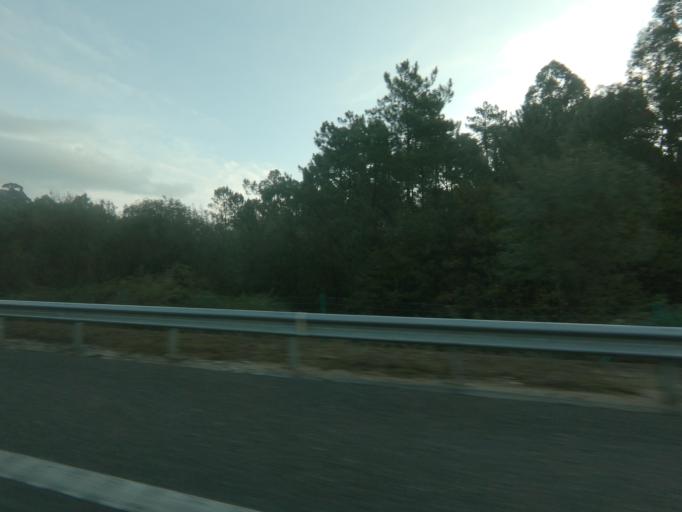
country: ES
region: Galicia
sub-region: Provincia de Pontevedra
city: Tui
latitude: 42.0990
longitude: -8.6438
